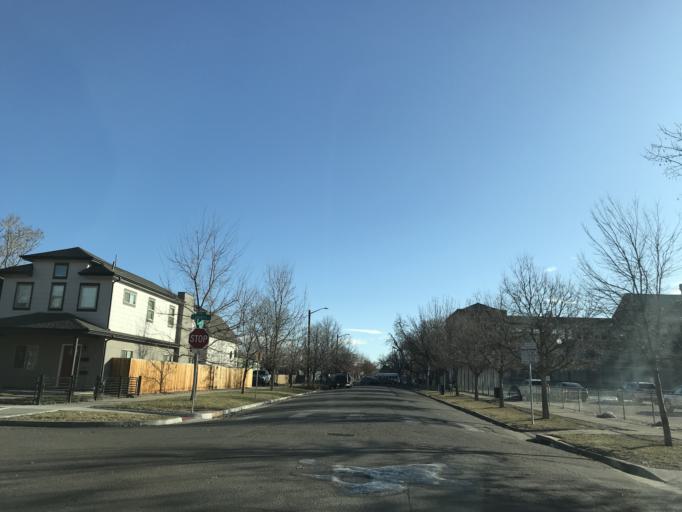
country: US
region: Colorado
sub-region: Denver County
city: Denver
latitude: 39.7636
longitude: -104.9715
